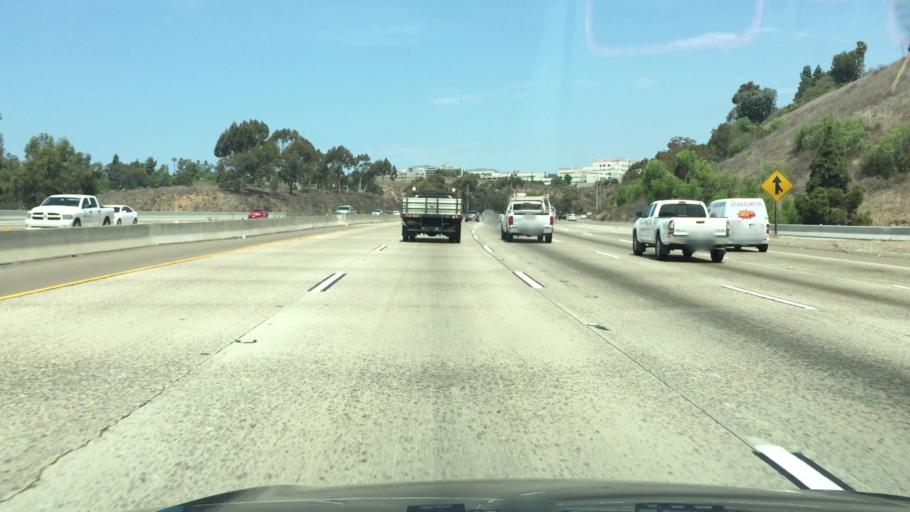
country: US
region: California
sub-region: San Diego County
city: San Diego
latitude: 32.7885
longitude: -117.1481
